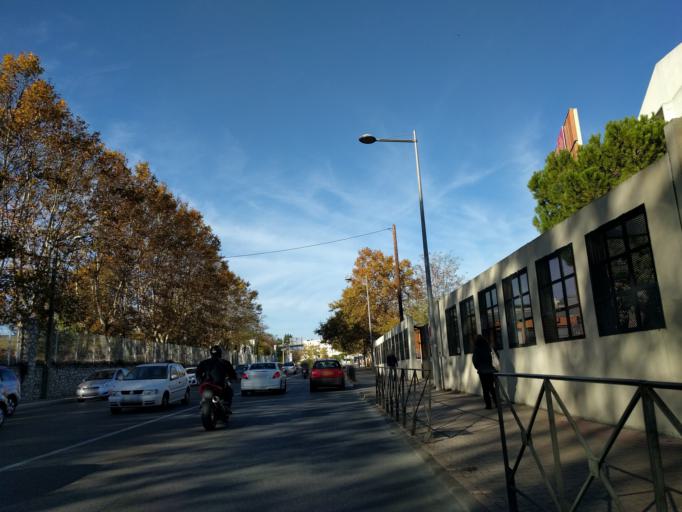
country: FR
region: Languedoc-Roussillon
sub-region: Departement de l'Herault
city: Montpellier
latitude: 43.6109
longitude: 3.8902
